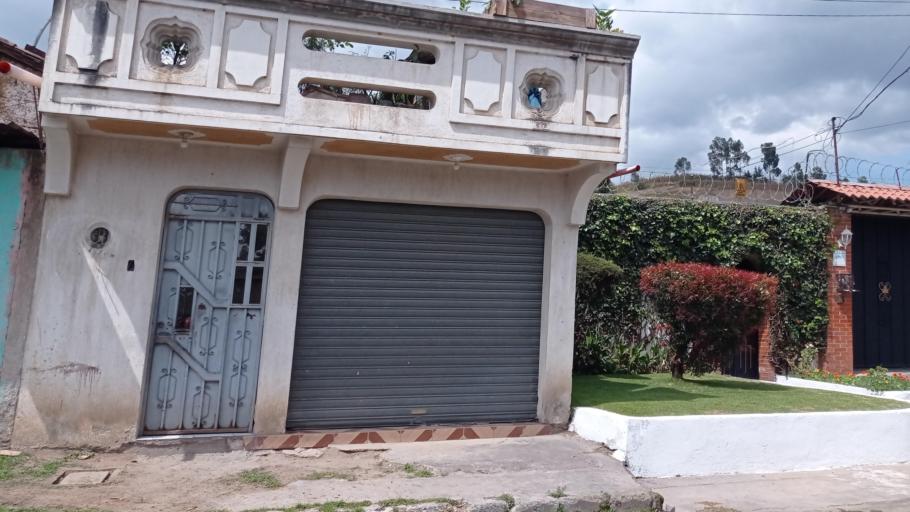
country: GT
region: Quetzaltenango
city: Quetzaltenango
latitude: 14.8534
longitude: -91.4935
